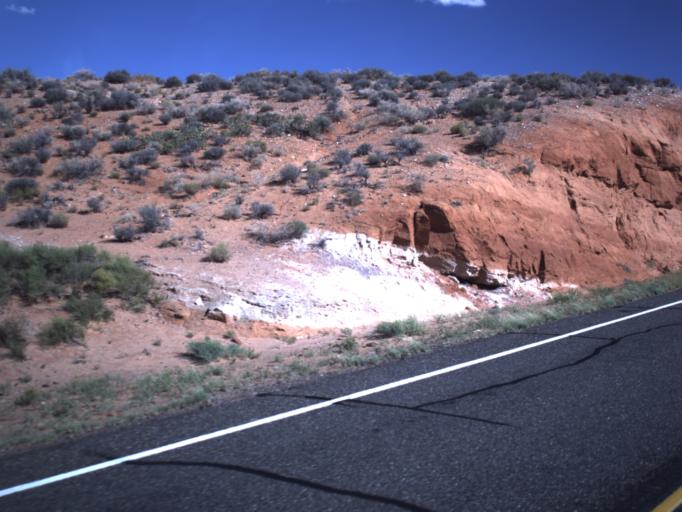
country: US
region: Utah
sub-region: Wayne County
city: Loa
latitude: 38.0692
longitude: -110.6057
